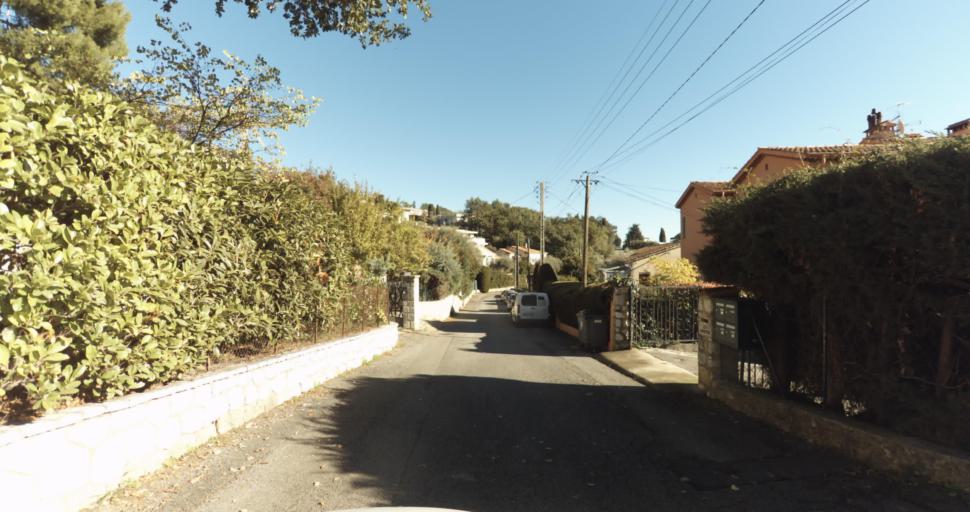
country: FR
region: Provence-Alpes-Cote d'Azur
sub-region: Departement des Alpes-Maritimes
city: Vence
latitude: 43.7200
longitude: 7.1022
